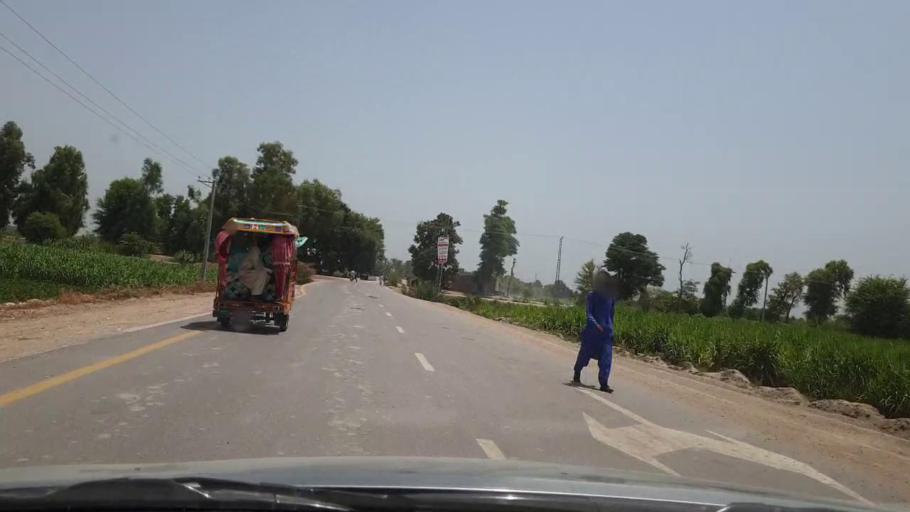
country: PK
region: Sindh
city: Pano Aqil
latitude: 27.8603
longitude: 69.0866
